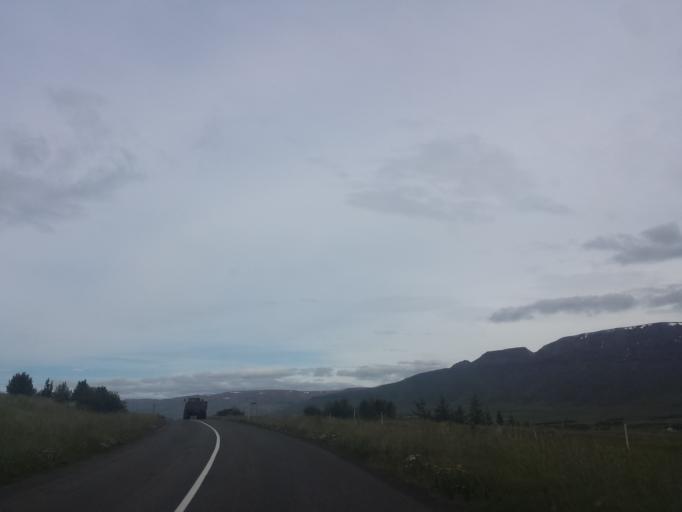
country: IS
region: Northeast
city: Akureyri
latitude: 65.5252
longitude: -18.1510
